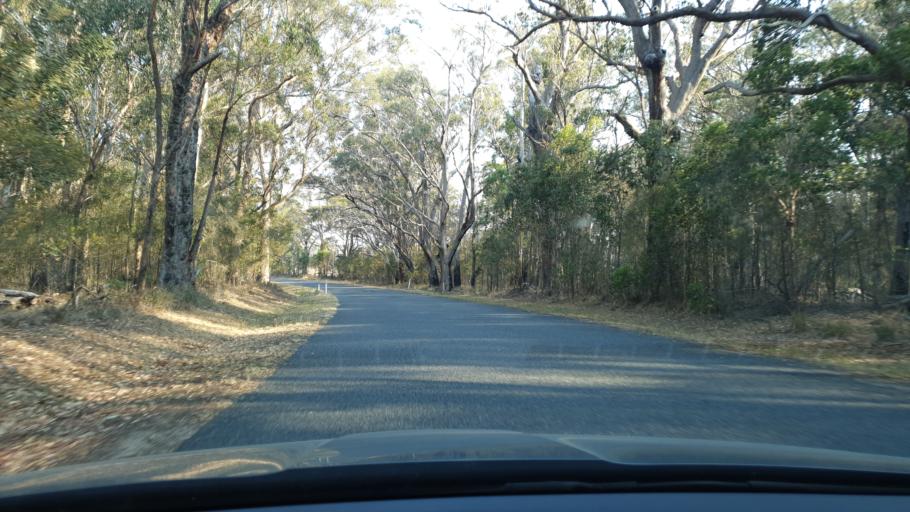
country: AU
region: New South Wales
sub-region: Tenterfield Municipality
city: Carrolls Creek
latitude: -28.6954
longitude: 152.0911
